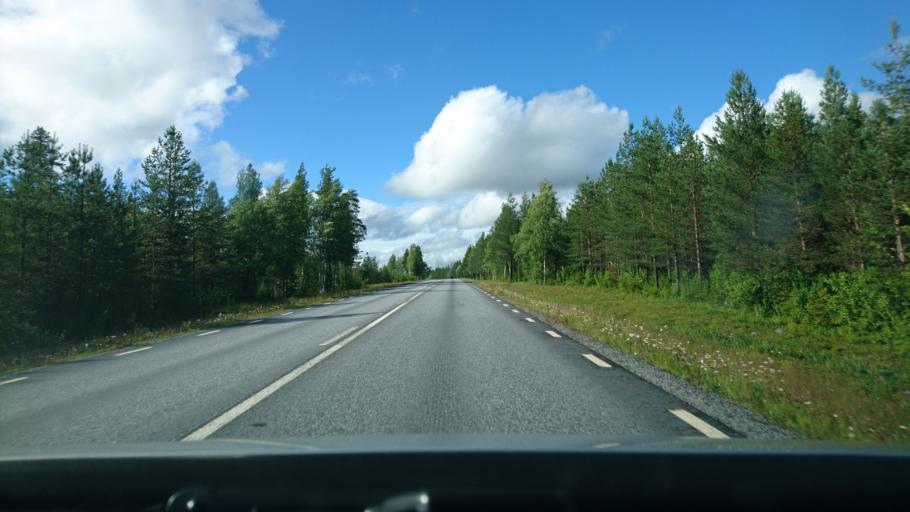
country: SE
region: Vaesterbotten
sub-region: Vilhelmina Kommun
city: Vilhelmina
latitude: 64.5940
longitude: 16.7335
